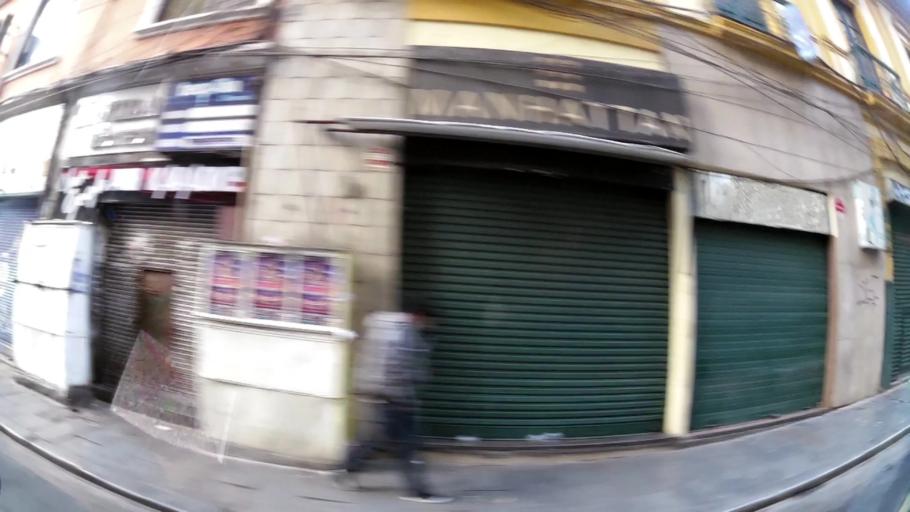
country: BO
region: La Paz
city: La Paz
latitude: -16.4968
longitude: -68.1340
